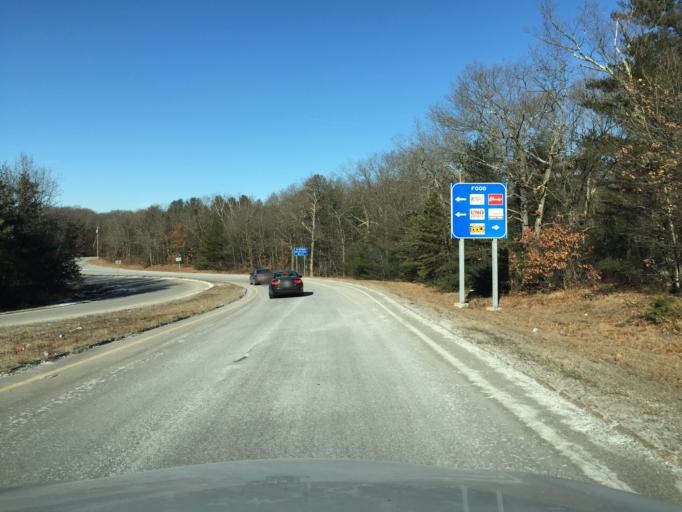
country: US
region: Massachusetts
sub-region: Norfolk County
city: Wrentham
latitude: 42.0408
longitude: -71.3422
